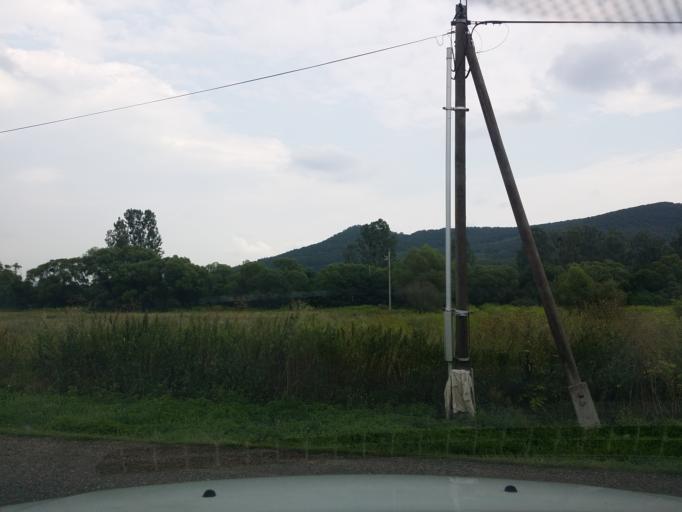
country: HU
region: Borsod-Abauj-Zemplen
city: Sarospatak
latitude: 48.4590
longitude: 21.5289
